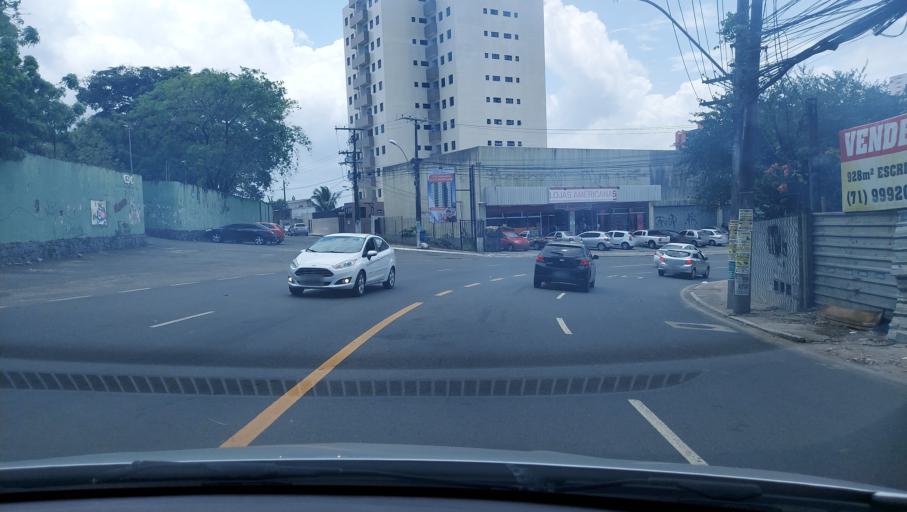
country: BR
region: Bahia
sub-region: Salvador
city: Salvador
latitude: -12.9581
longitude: -38.4672
